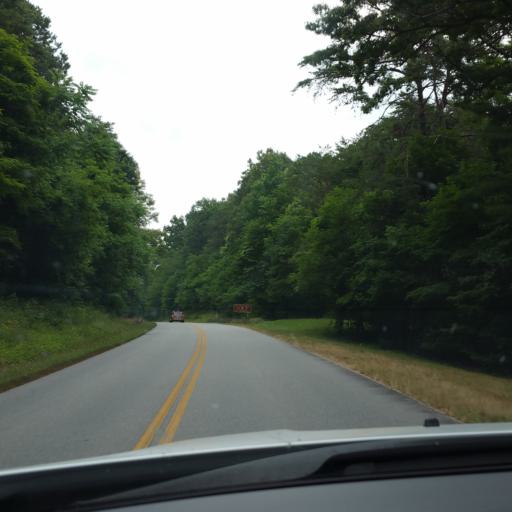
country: US
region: North Carolina
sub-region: Buncombe County
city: Biltmore Forest
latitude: 35.5663
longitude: -82.4848
